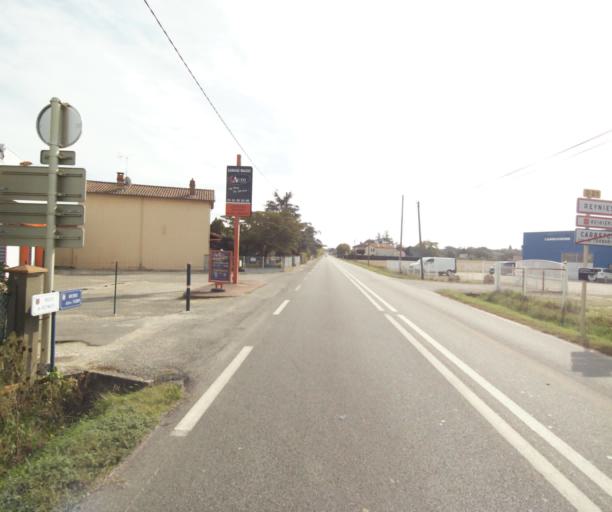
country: FR
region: Midi-Pyrenees
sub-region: Departement du Tarn-et-Garonne
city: Orgueil
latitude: 43.9225
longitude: 1.3929
